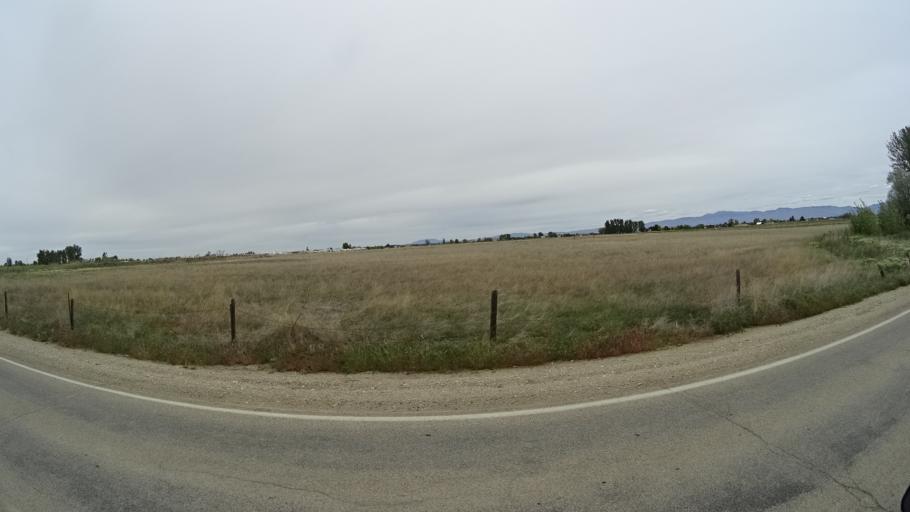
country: US
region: Idaho
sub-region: Ada County
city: Kuna
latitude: 43.4879
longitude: -116.3888
